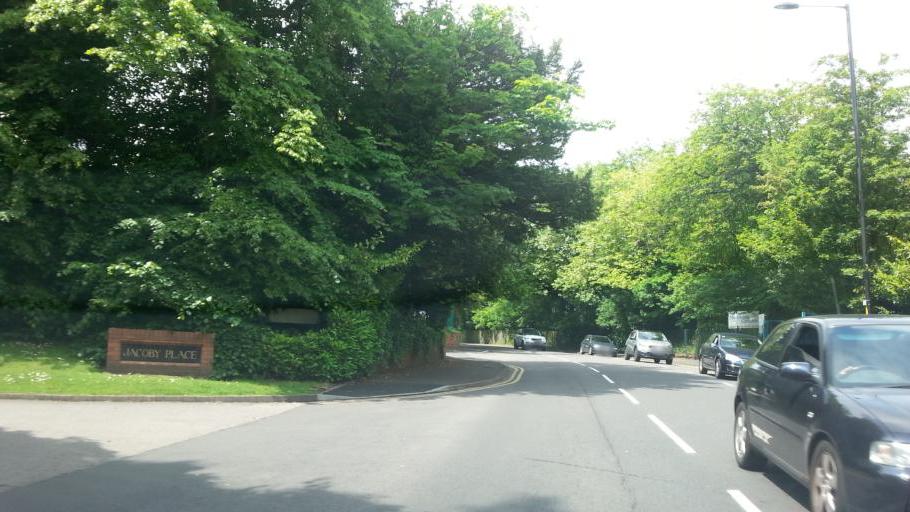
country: GB
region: England
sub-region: City and Borough of Birmingham
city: Birmingham
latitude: 52.4563
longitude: -1.9117
